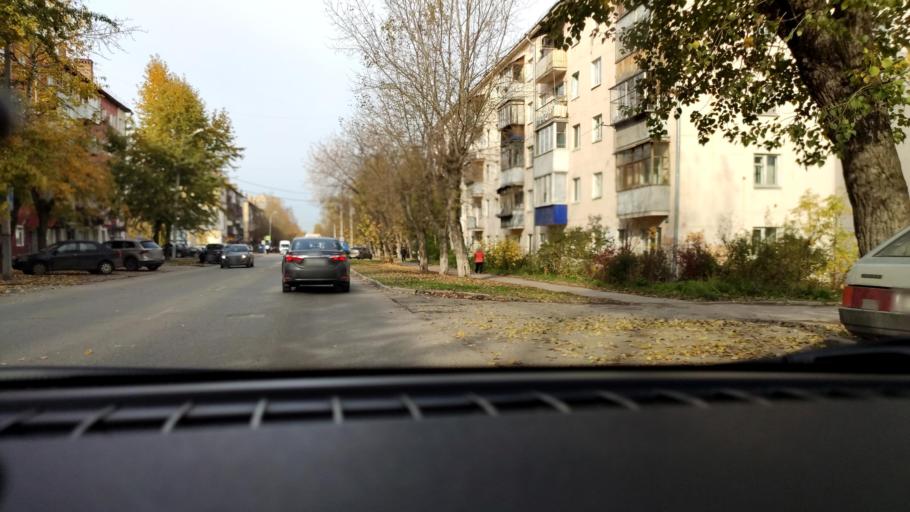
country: RU
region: Perm
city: Perm
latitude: 58.1031
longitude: 56.3876
